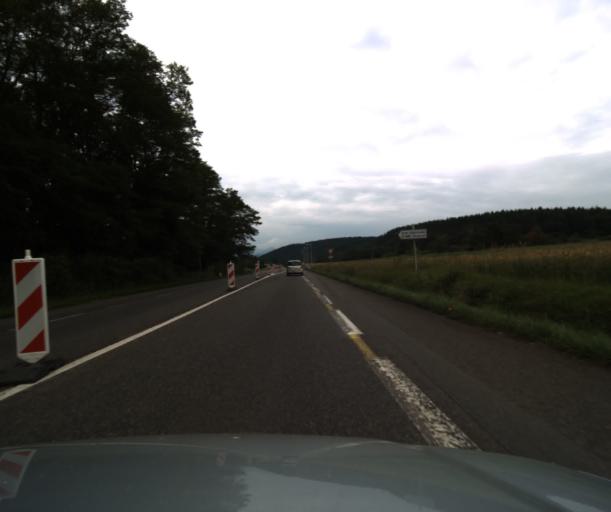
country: FR
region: Midi-Pyrenees
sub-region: Departement des Hautes-Pyrenees
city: Ossun
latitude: 43.1599
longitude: -0.0162
